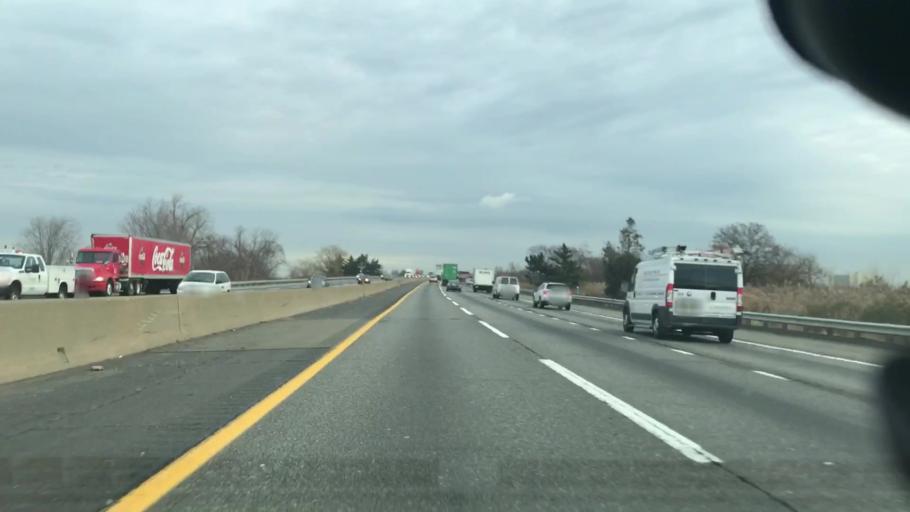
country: US
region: New Jersey
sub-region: Hudson County
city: Secaucus
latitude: 40.7896
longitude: -74.0882
